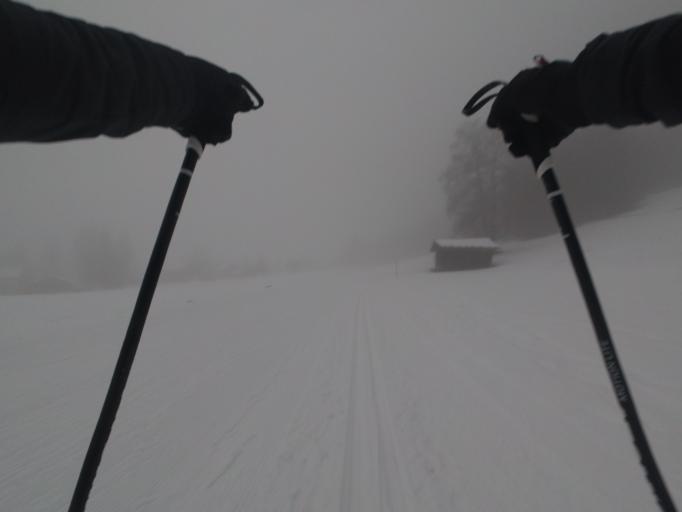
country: AT
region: Salzburg
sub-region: Politischer Bezirk Sankt Johann im Pongau
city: Wagrain
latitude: 47.3405
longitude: 13.3087
